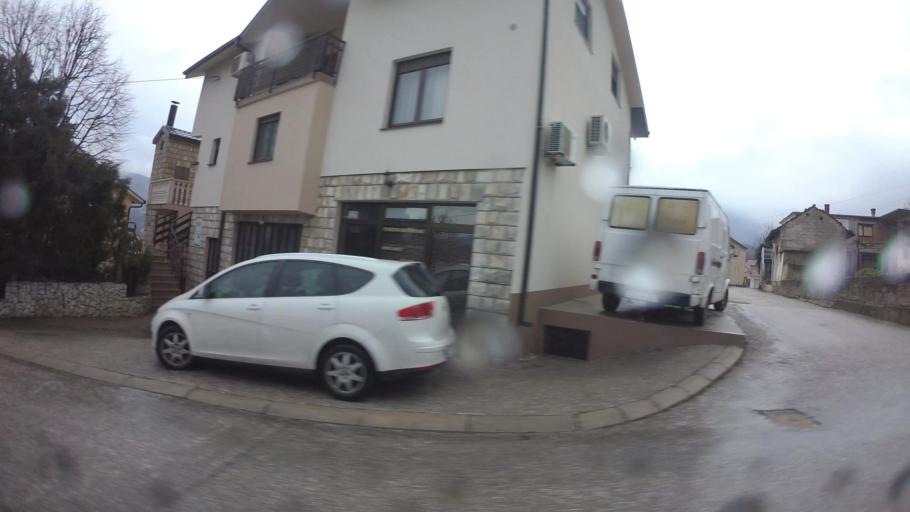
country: BA
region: Federation of Bosnia and Herzegovina
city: Cim
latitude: 43.3536
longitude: 17.7764
